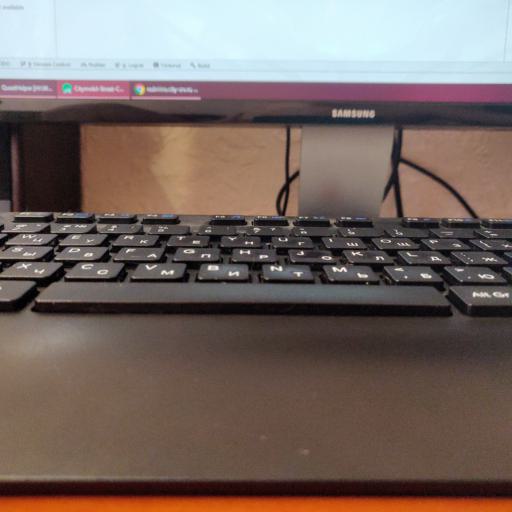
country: FI
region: Haeme
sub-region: Forssa
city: Jokioinen
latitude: 60.9015
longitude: 23.5057
